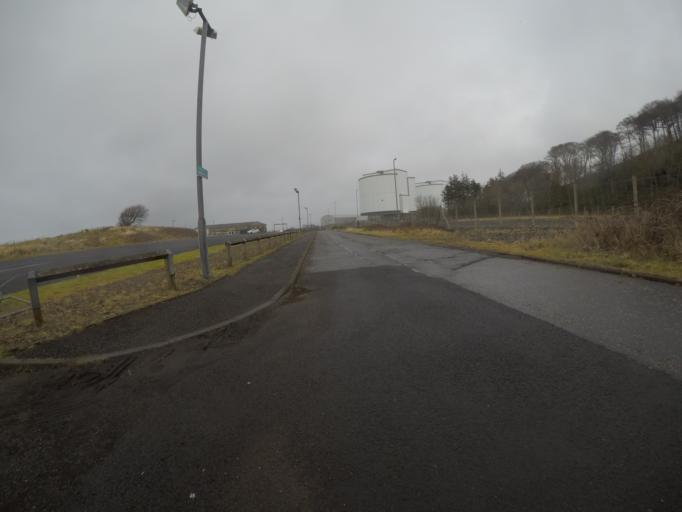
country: GB
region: Scotland
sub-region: North Ayrshire
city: Millport
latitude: 55.7176
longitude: -4.9009
